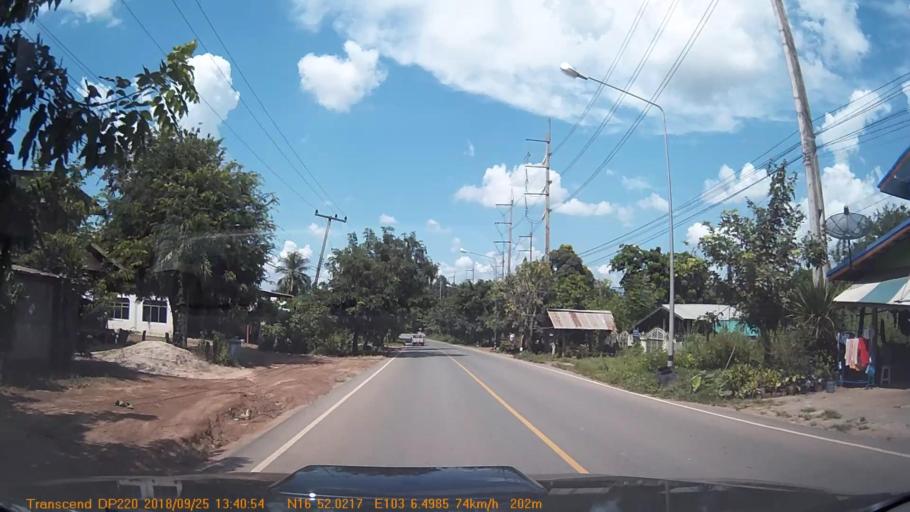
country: TH
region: Changwat Udon Thani
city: Si That
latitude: 16.8671
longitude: 103.1083
